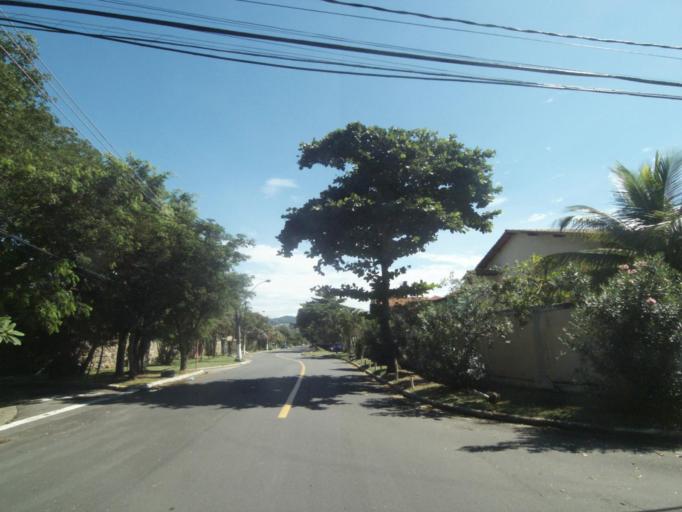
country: BR
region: Rio de Janeiro
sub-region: Niteroi
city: Niteroi
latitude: -22.9577
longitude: -43.0571
